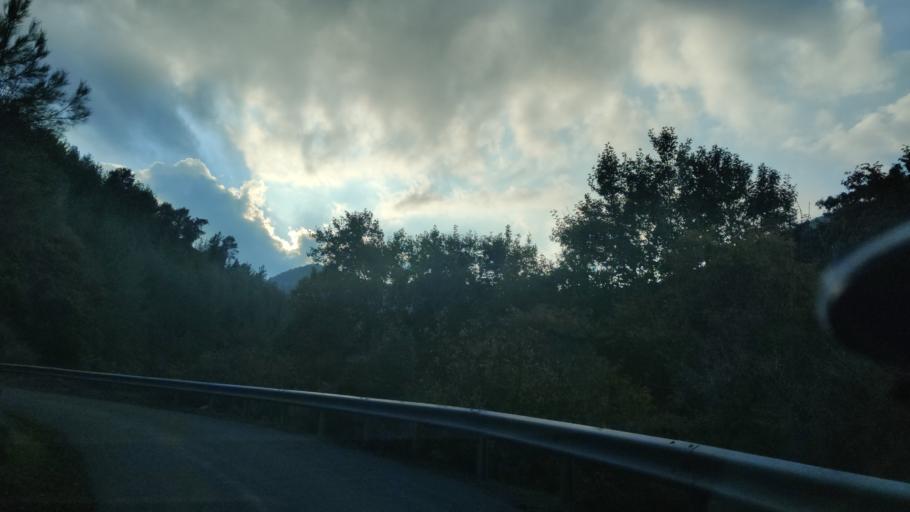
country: CY
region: Lefkosia
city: Lefka
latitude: 35.0702
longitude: 32.7417
